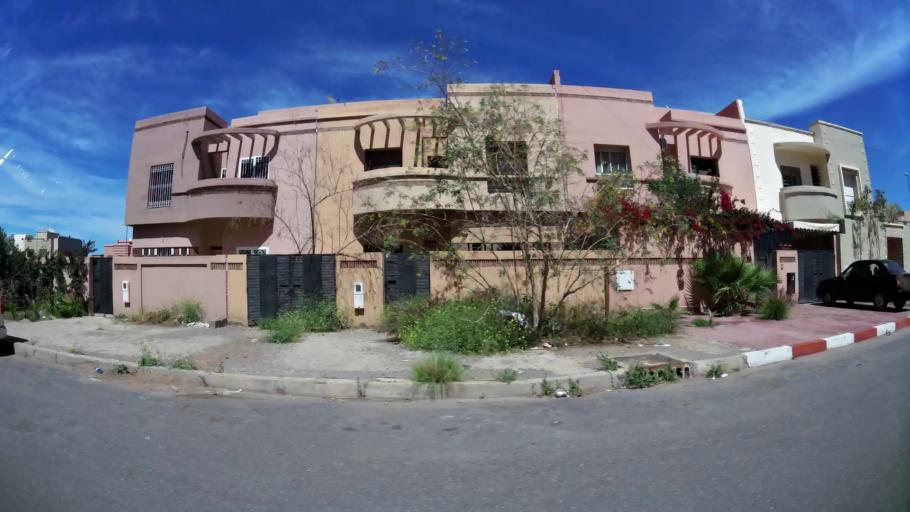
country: MA
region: Marrakech-Tensift-Al Haouz
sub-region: Marrakech
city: Marrakesh
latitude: 31.6474
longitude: -8.0723
